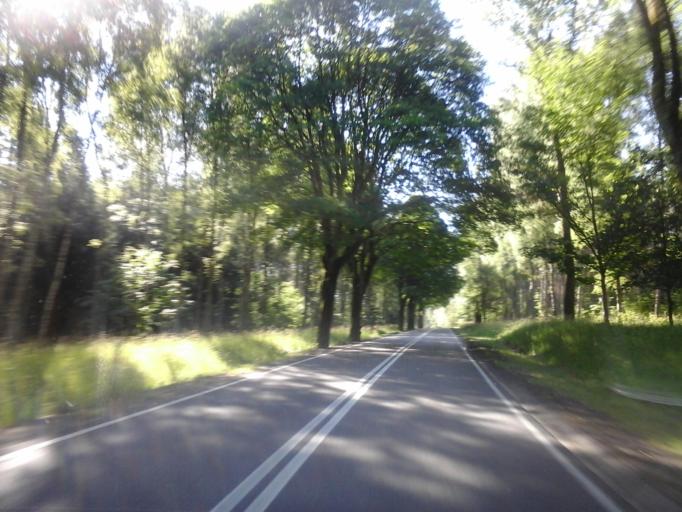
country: PL
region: West Pomeranian Voivodeship
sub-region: Powiat drawski
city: Drawsko Pomorskie
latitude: 53.4935
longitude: 15.7047
